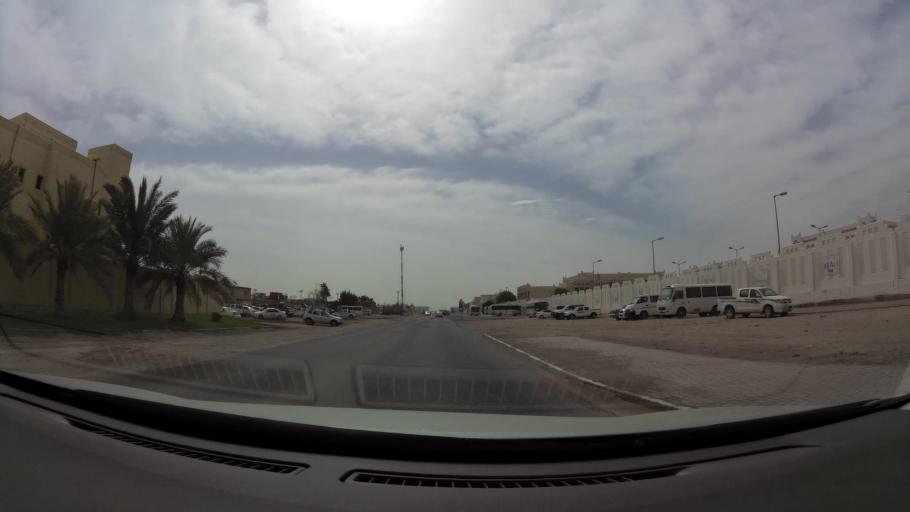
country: QA
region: Baladiyat ad Dawhah
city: Doha
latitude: 25.2236
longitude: 51.4890
